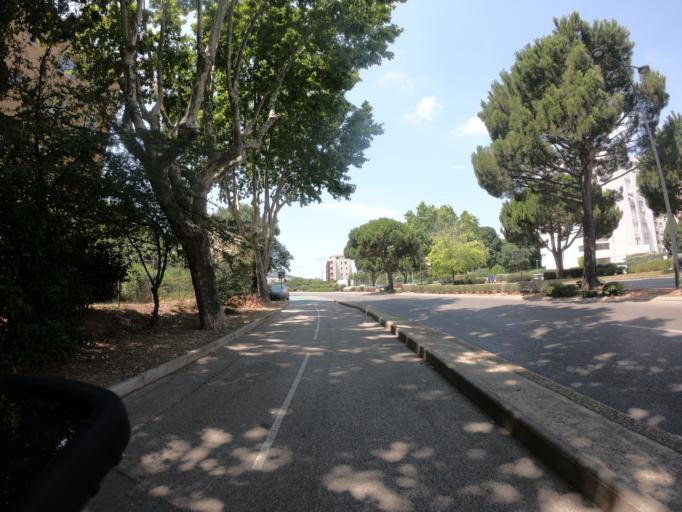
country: FR
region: Provence-Alpes-Cote d'Azur
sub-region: Departement du Var
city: Six-Fours-les-Plages
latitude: 43.1079
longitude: 5.8663
